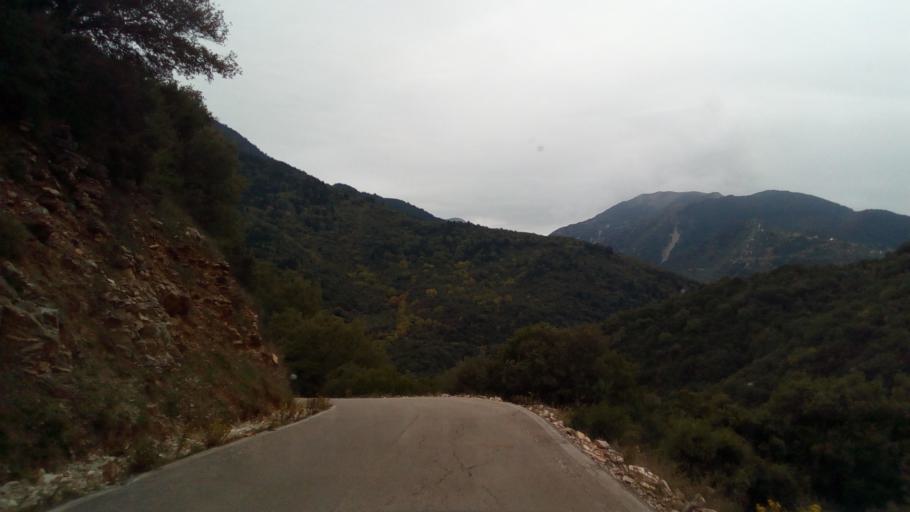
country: GR
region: West Greece
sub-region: Nomos Aitolias kai Akarnanias
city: Thermo
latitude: 38.6002
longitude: 21.8440
